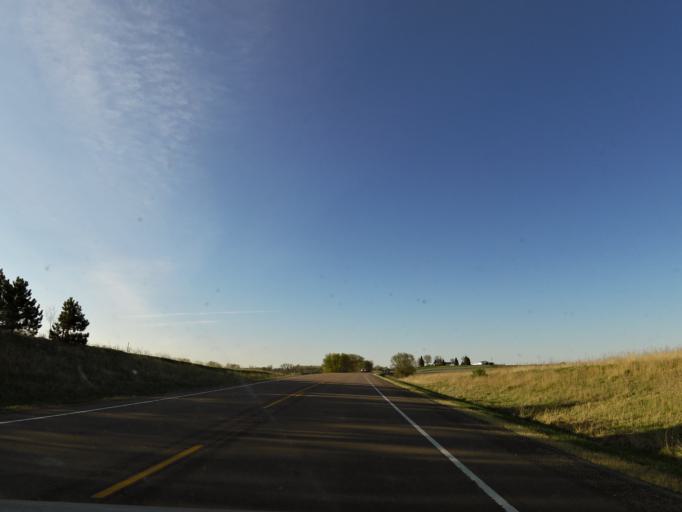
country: US
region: Minnesota
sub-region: Goodhue County
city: Cannon Falls
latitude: 44.5894
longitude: -92.9948
